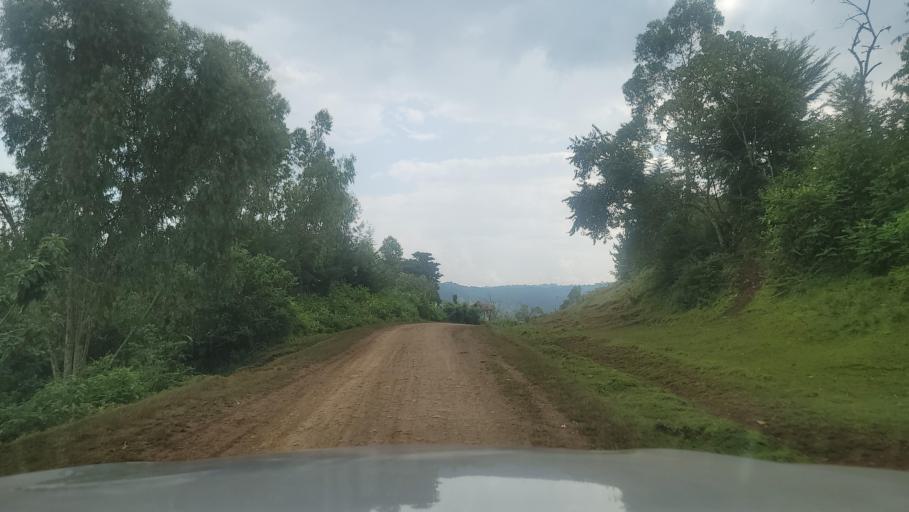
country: ET
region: Southern Nations, Nationalities, and People's Region
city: Bonga
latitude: 7.6982
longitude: 36.2472
